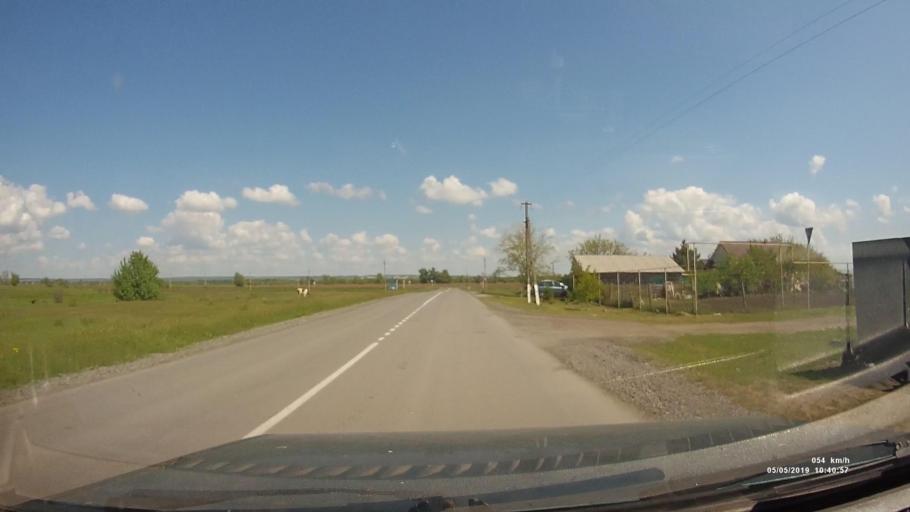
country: RU
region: Rostov
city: Ust'-Donetskiy
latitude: 47.5881
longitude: 40.8429
